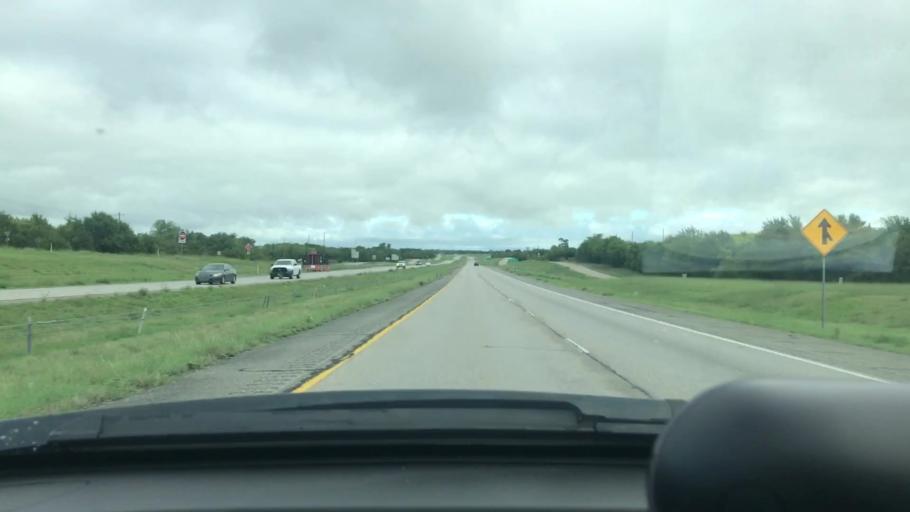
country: US
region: Texas
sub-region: Grayson County
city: Van Alstyne
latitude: 33.3825
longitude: -96.5807
